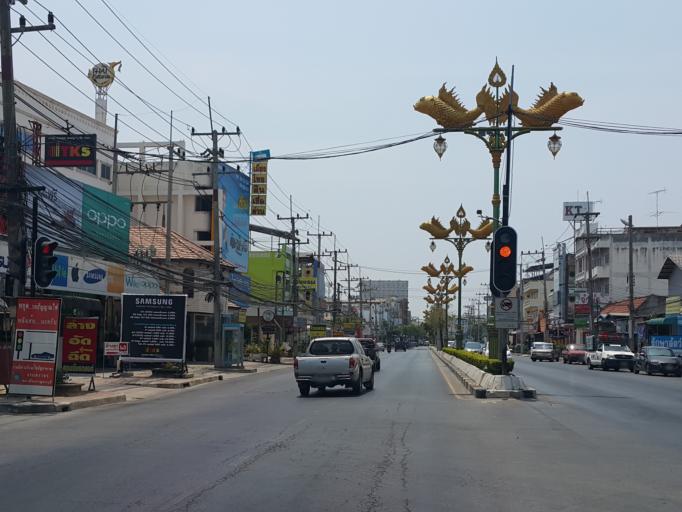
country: TH
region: Kanchanaburi
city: Kanchanaburi
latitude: 14.0304
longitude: 99.5278
